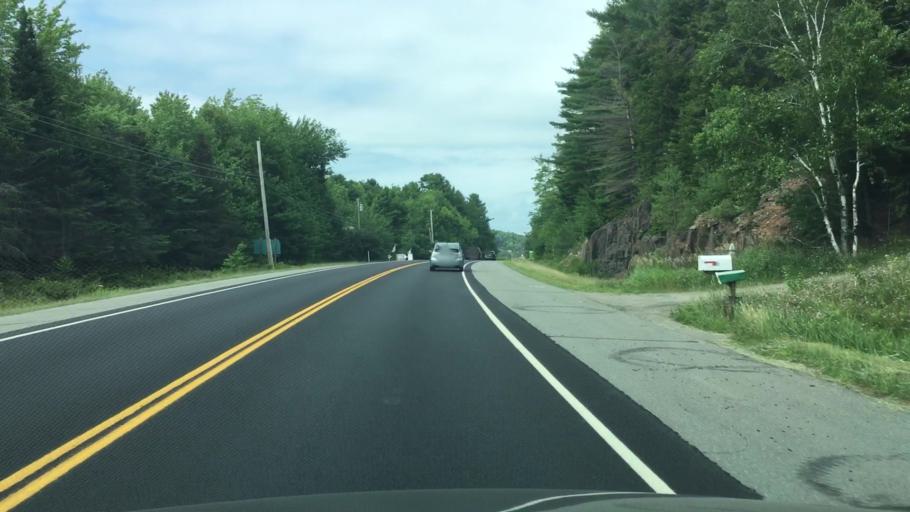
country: US
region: Maine
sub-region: Hancock County
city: Bucksport
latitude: 44.5422
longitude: -68.8098
